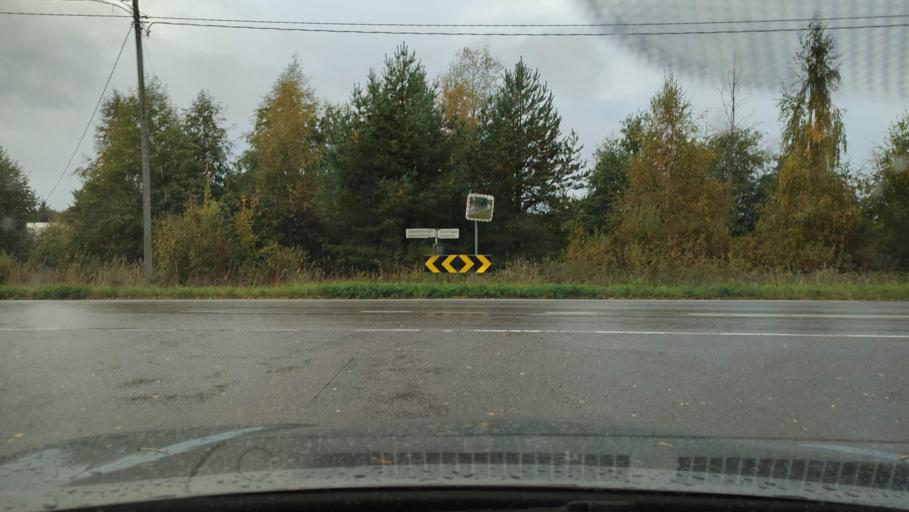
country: FI
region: Southern Ostrobothnia
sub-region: Suupohja
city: Karijoki
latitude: 62.2329
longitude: 21.6531
